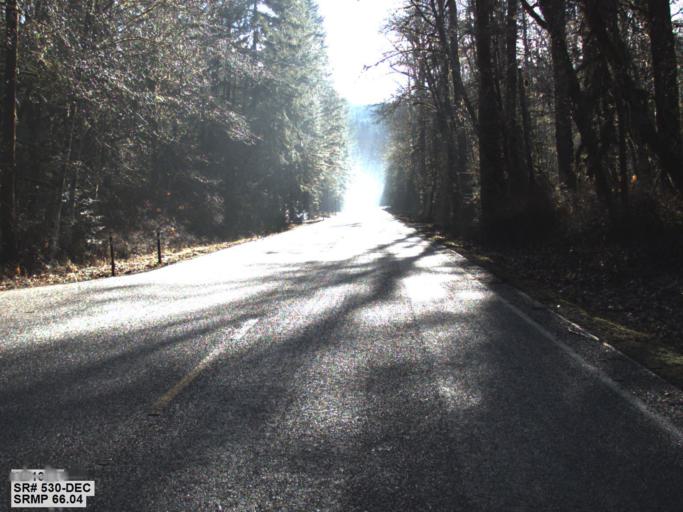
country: US
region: Washington
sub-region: Snohomish County
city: Darrington
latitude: 48.4658
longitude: -121.5870
